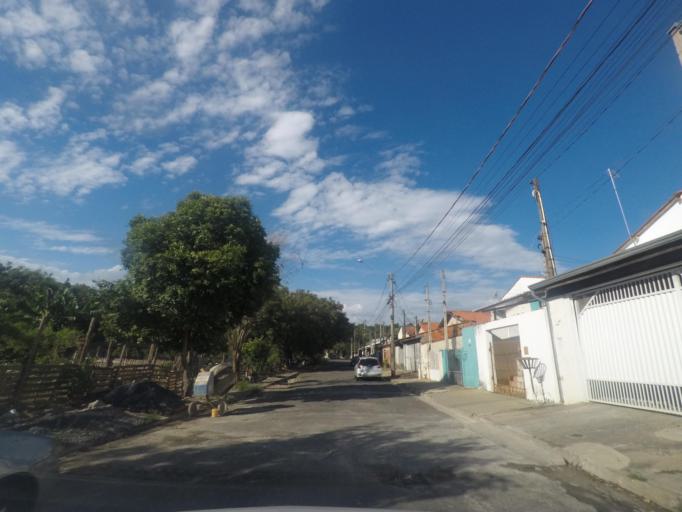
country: BR
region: Sao Paulo
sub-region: Sumare
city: Sumare
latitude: -22.8122
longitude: -47.2623
